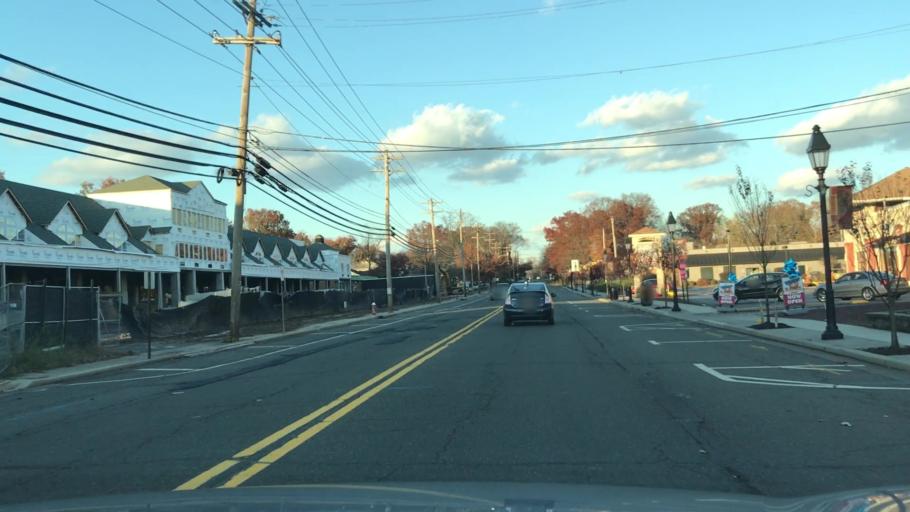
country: US
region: New Jersey
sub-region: Bergen County
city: Norwood
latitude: 40.9989
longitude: -73.9542
